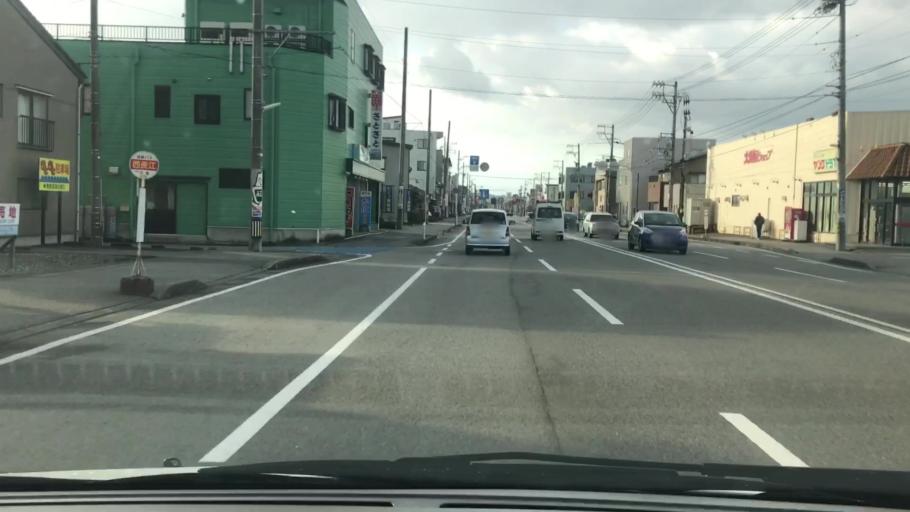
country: JP
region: Toyama
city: Toyama-shi
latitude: 36.6869
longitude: 137.2402
